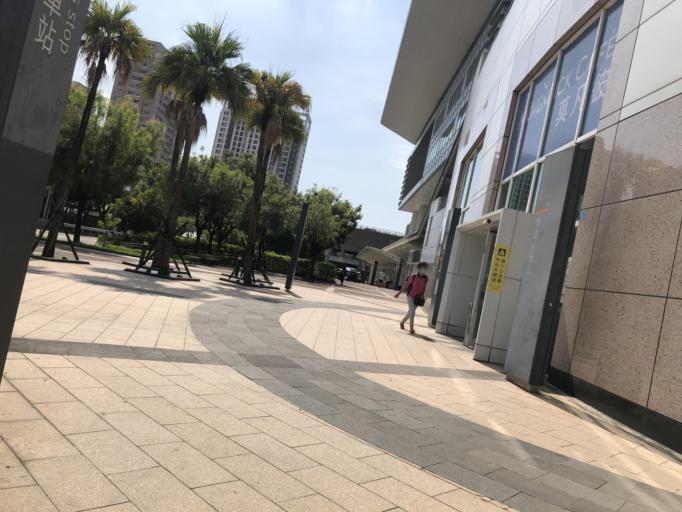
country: TW
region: Kaohsiung
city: Kaohsiung
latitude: 22.6864
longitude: 120.3085
